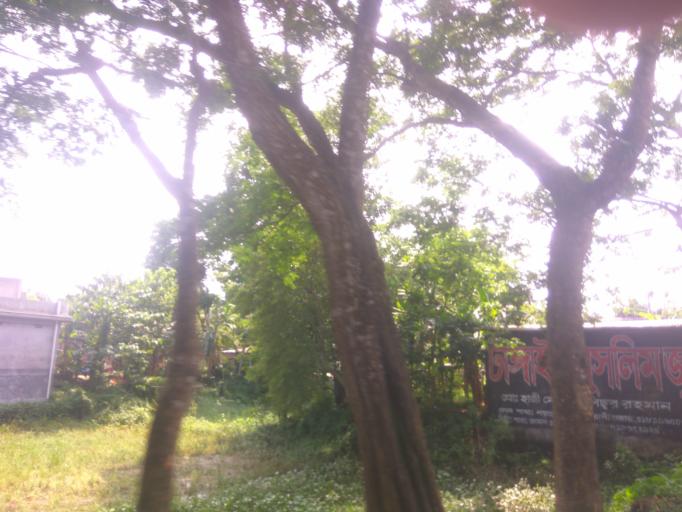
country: IN
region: Assam
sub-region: Karimganj
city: Karimganj
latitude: 24.8093
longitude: 92.1833
